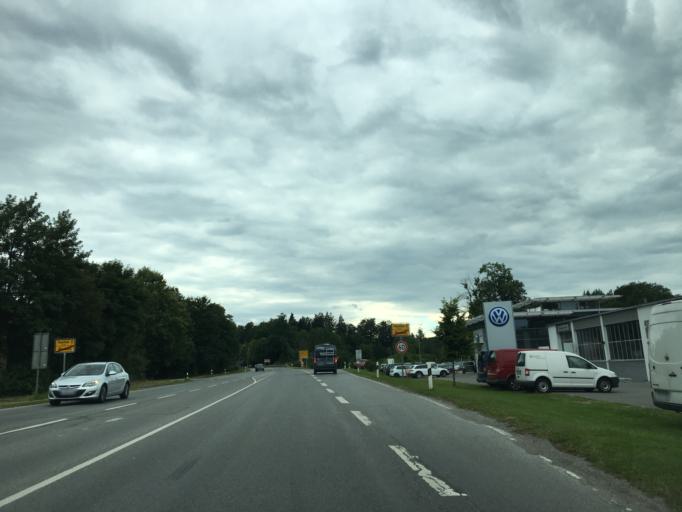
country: DE
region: Bavaria
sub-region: Upper Bavaria
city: Miesbach
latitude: 47.7821
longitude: 11.8330
